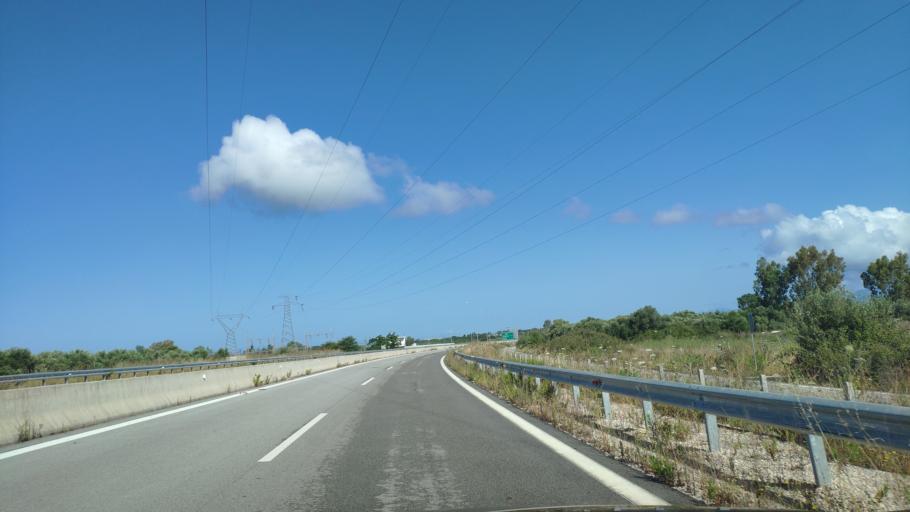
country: GR
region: Epirus
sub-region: Nomos Prevezis
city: Preveza
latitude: 38.9136
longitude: 20.7965
